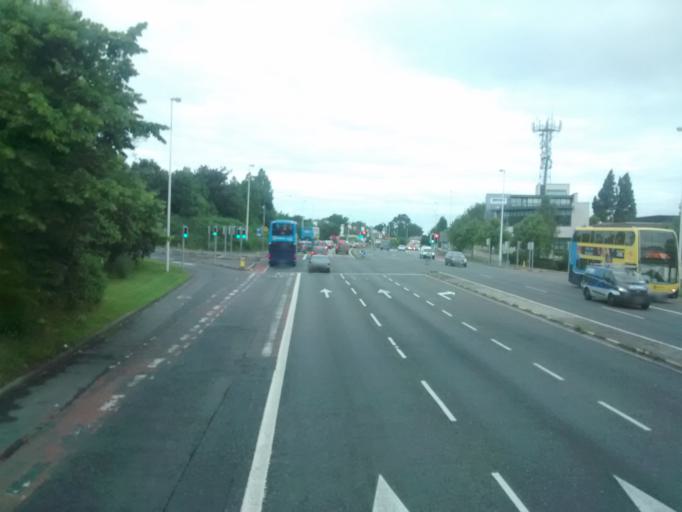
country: IE
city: Booterstown
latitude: 53.2925
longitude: -6.2006
